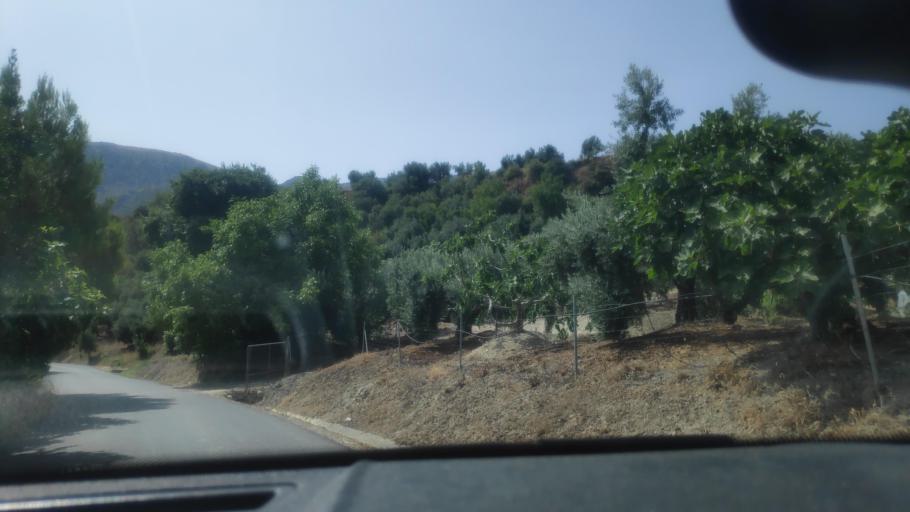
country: ES
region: Andalusia
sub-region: Provincia de Jaen
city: Torres
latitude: 37.7882
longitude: -3.4615
